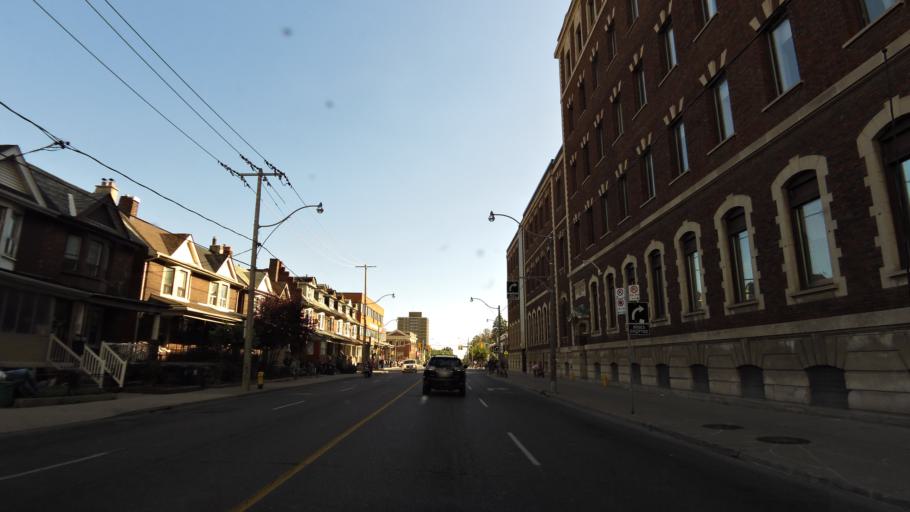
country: CA
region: Ontario
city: Toronto
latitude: 43.6609
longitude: -79.4359
